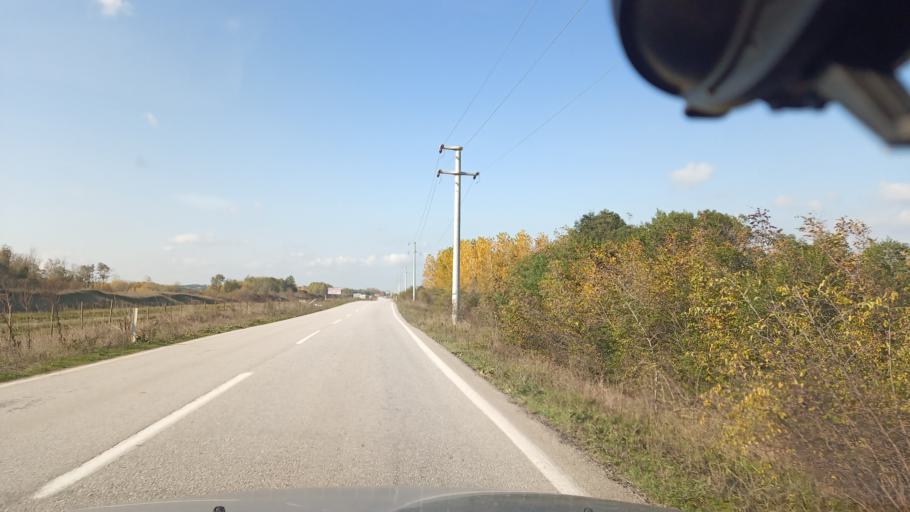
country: TR
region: Sakarya
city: Karasu
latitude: 41.1211
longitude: 30.5878
